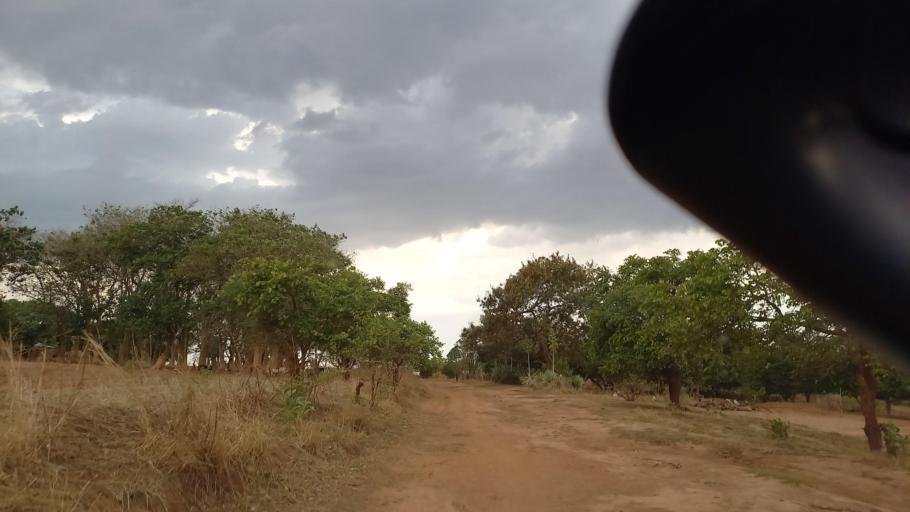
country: ZM
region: Lusaka
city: Kafue
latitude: -16.1323
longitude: 28.0578
